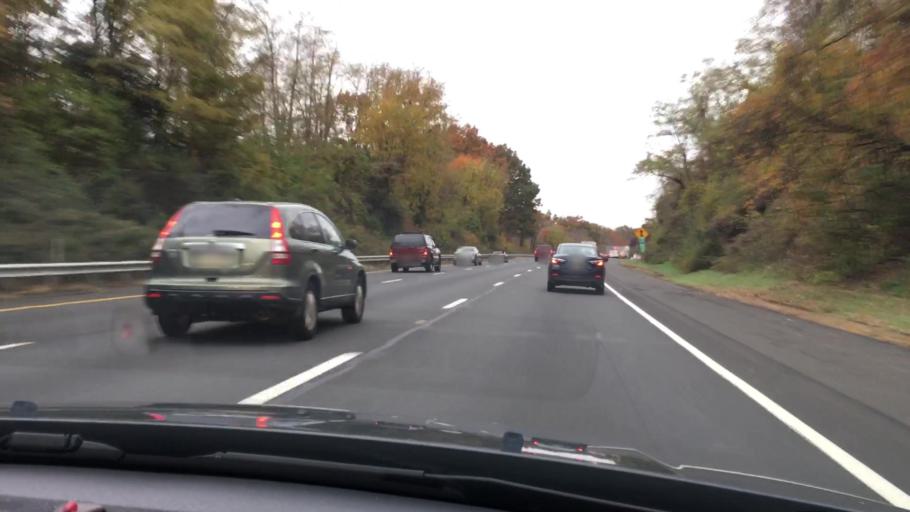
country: US
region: New Jersey
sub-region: Somerset County
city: Bernardsville
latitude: 40.7281
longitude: -74.5403
